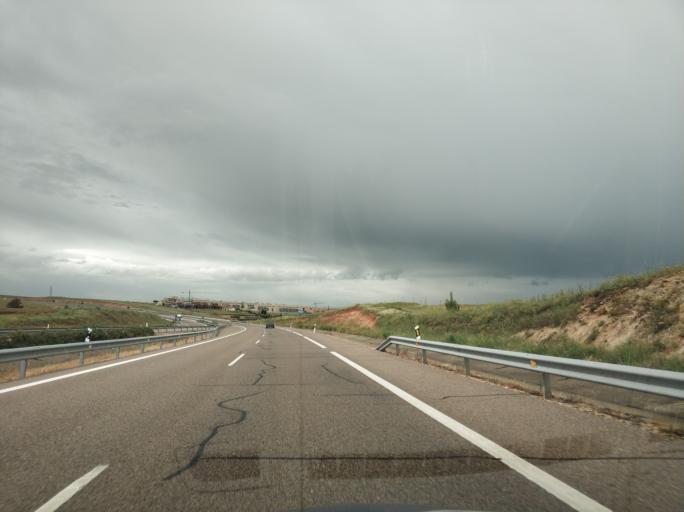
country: ES
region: Castille and Leon
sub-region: Provincia de Salamanca
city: Aldeatejada
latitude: 40.9354
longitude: -5.6801
